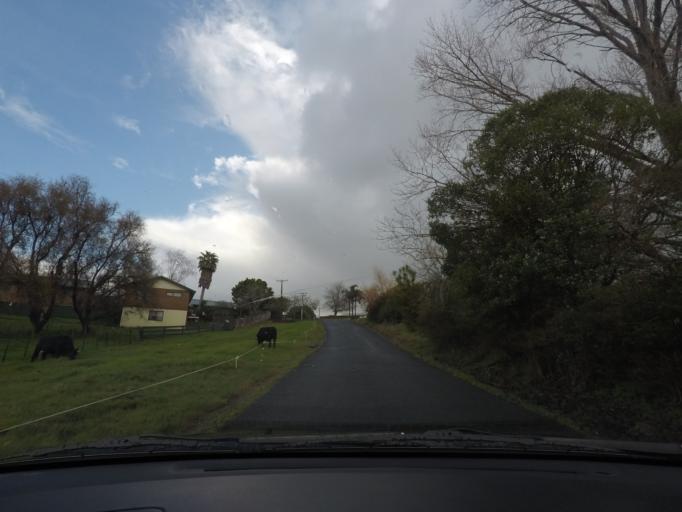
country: NZ
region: Auckland
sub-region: Auckland
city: Warkworth
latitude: -36.4301
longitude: 174.7316
